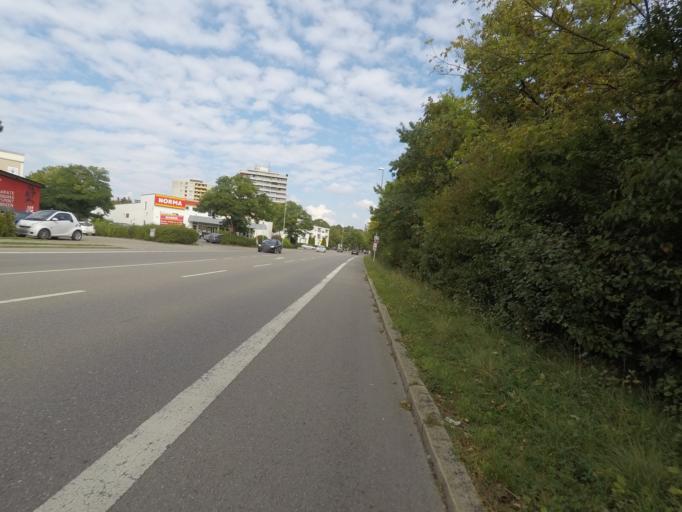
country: DE
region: Baden-Wuerttemberg
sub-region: Tuebingen Region
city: Reutlingen
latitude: 48.5091
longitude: 9.2172
